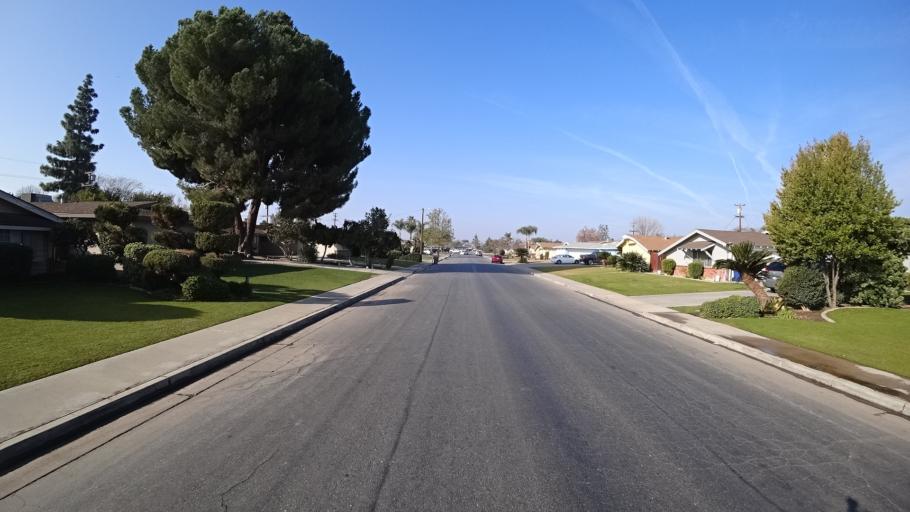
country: US
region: California
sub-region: Kern County
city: Bakersfield
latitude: 35.3282
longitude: -119.0283
